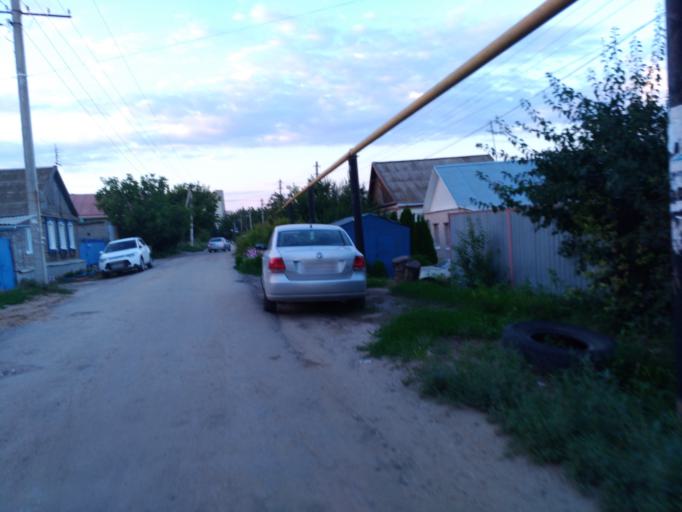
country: RU
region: Volgograd
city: Volgograd
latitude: 48.6707
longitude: 44.4506
